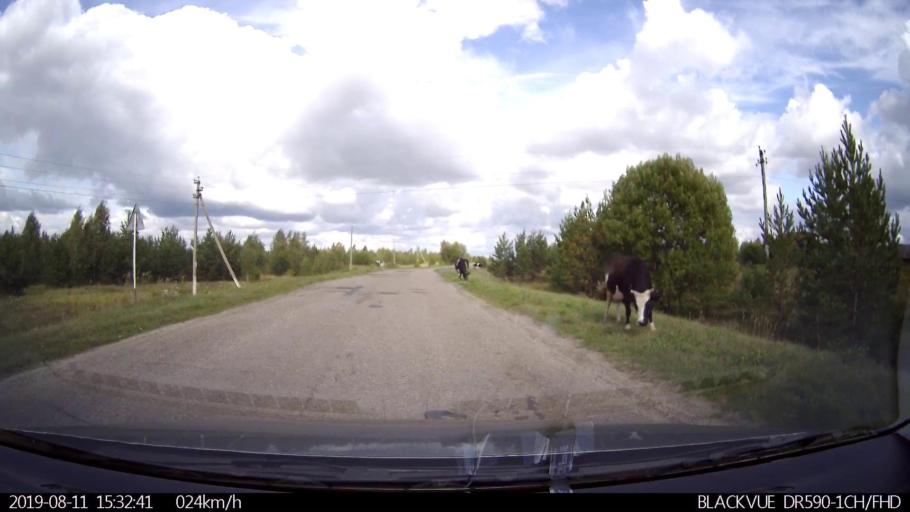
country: RU
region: Ulyanovsk
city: Ignatovka
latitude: 53.8607
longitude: 47.5769
